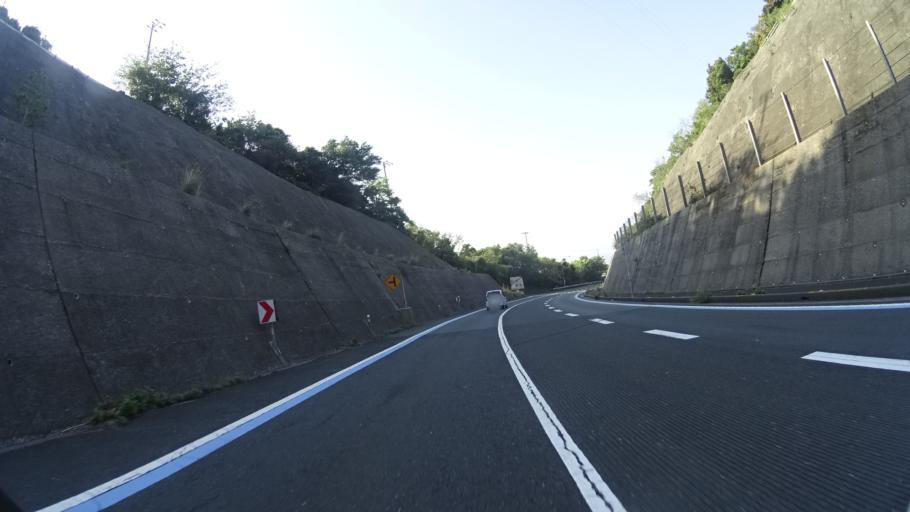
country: JP
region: Ehime
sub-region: Nishiuwa-gun
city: Ikata-cho
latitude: 33.4101
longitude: 132.1731
